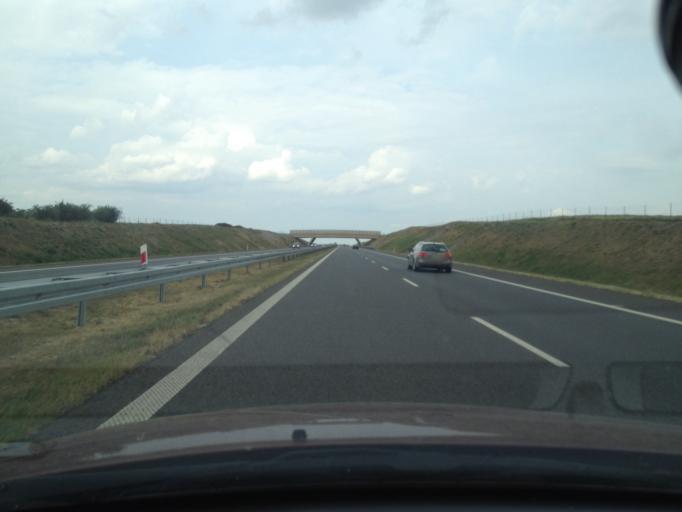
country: PL
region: West Pomeranian Voivodeship
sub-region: Powiat pyrzycki
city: Kozielice
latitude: 53.0635
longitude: 14.8630
